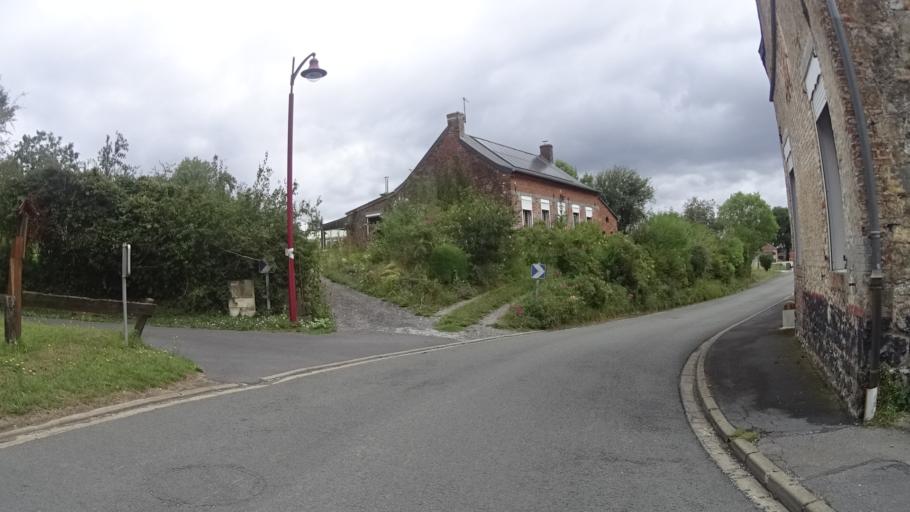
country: FR
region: Nord-Pas-de-Calais
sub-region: Departement du Nord
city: Berlaimont
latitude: 50.1788
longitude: 3.8041
